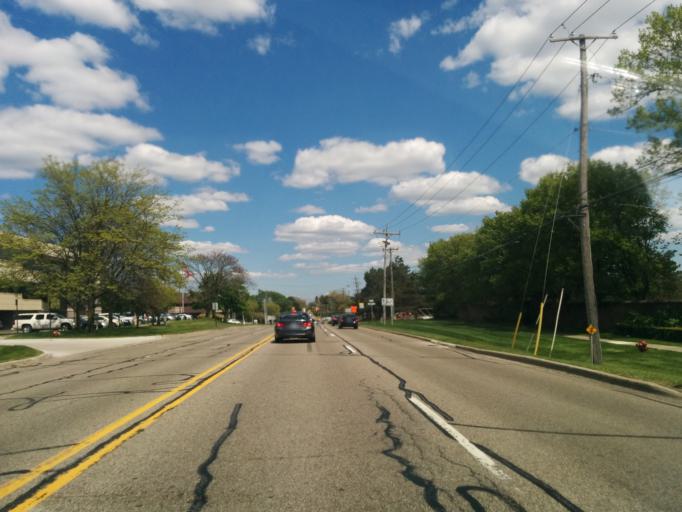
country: US
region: Michigan
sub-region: Oakland County
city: Franklin
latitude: 42.5144
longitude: -83.3352
